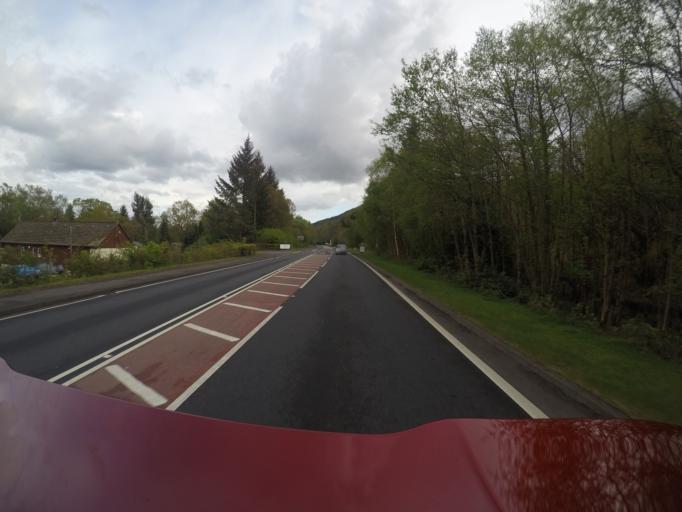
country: GB
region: Scotland
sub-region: Argyll and Bute
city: Helensburgh
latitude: 56.1474
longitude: -4.6648
